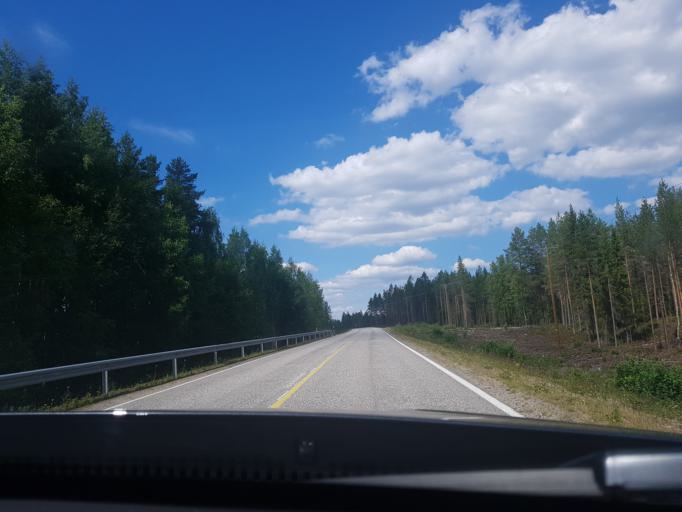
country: FI
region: Kainuu
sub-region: Kehys-Kainuu
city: Kuhmo
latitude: 64.2385
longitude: 29.8152
